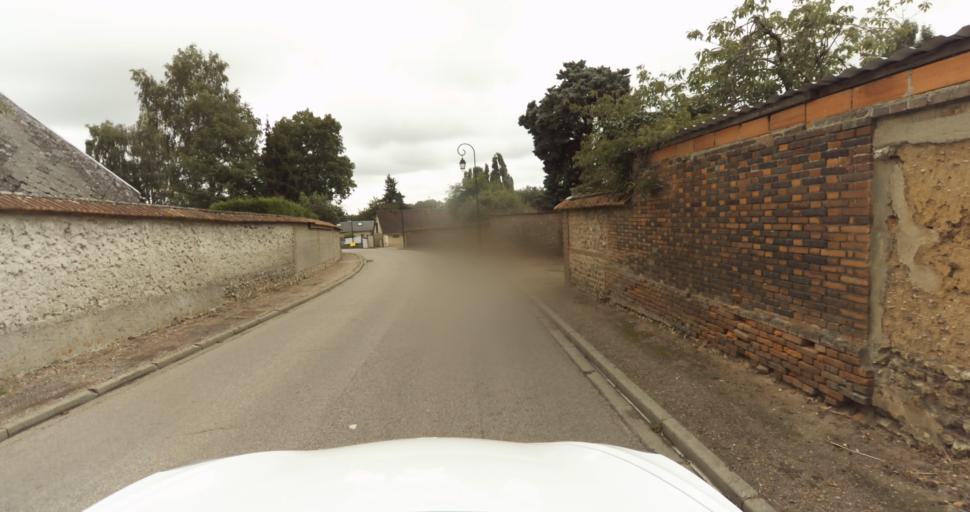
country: FR
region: Haute-Normandie
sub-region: Departement de l'Eure
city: Aviron
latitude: 49.0467
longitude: 1.0868
